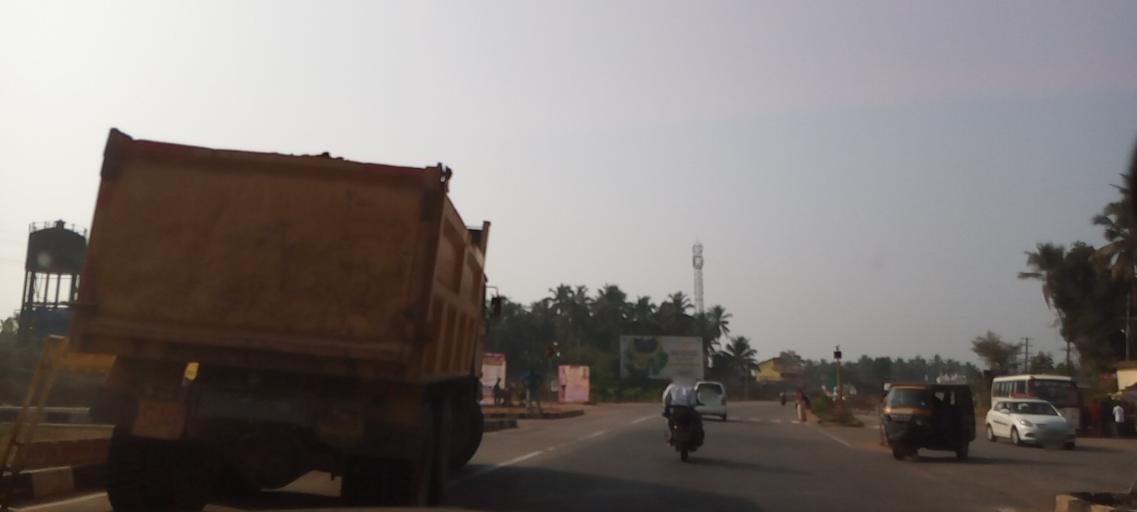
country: IN
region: Karnataka
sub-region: Udupi
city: Coondapoor
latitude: 13.6562
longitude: 74.7088
